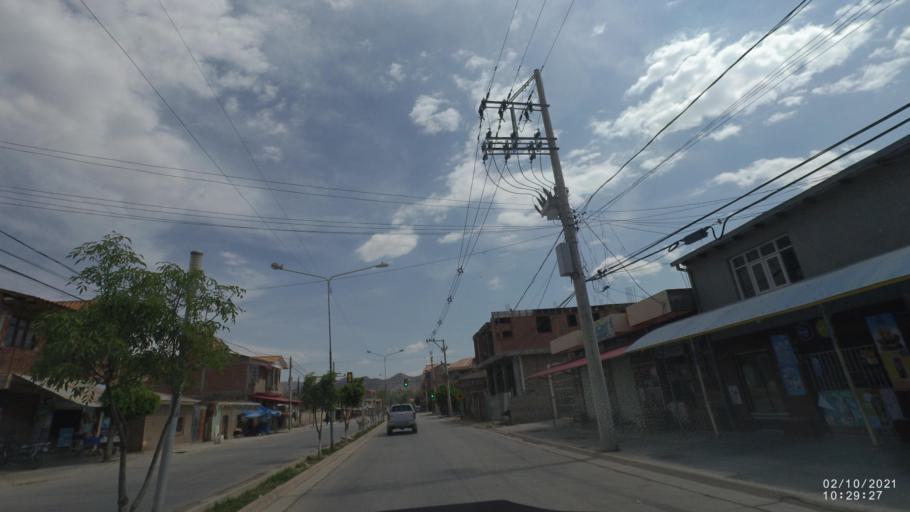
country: BO
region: Cochabamba
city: Capinota
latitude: -17.7053
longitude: -66.2658
